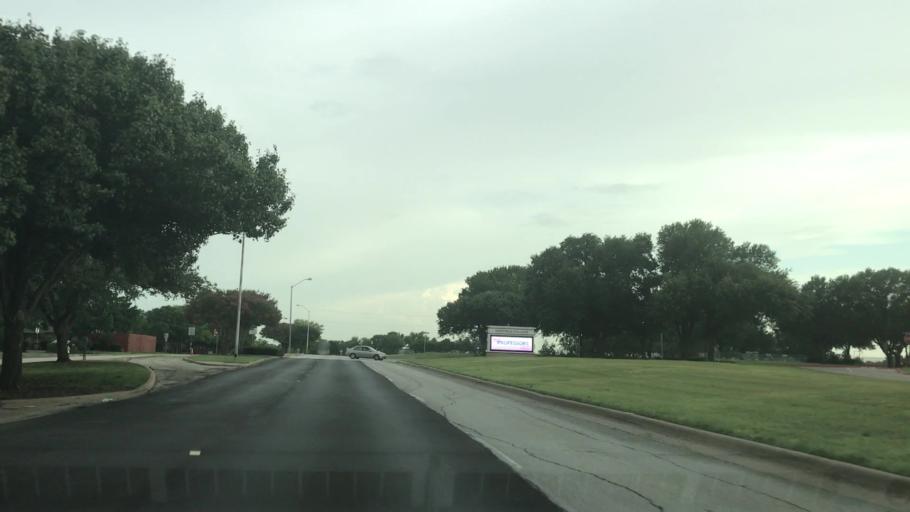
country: US
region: Texas
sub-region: Dallas County
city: Mesquite
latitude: 32.8156
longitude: -96.6569
